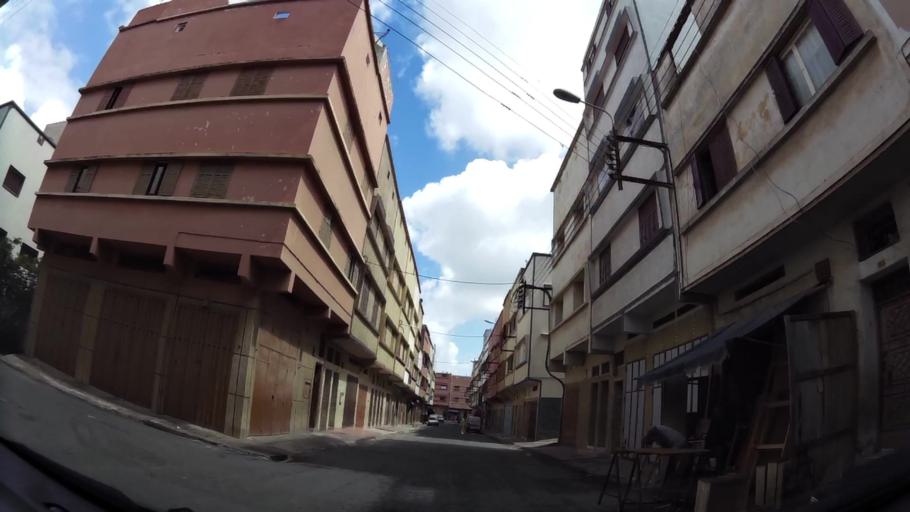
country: MA
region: Grand Casablanca
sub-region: Casablanca
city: Casablanca
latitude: 33.5383
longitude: -7.5854
